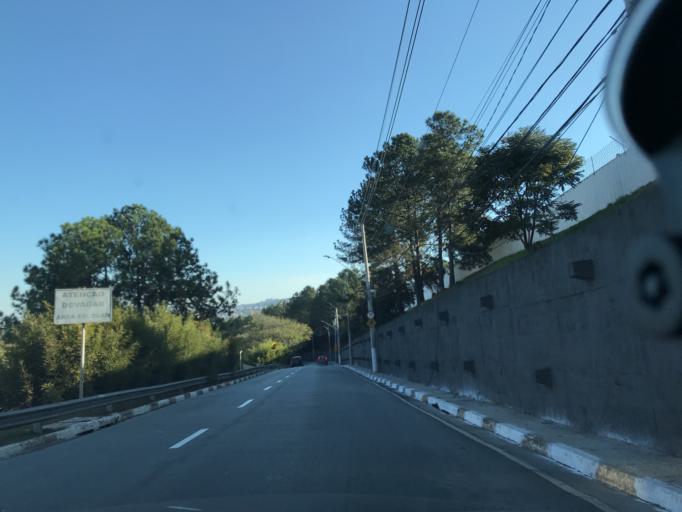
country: BR
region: Sao Paulo
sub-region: Barueri
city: Barueri
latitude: -23.4674
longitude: -46.8702
